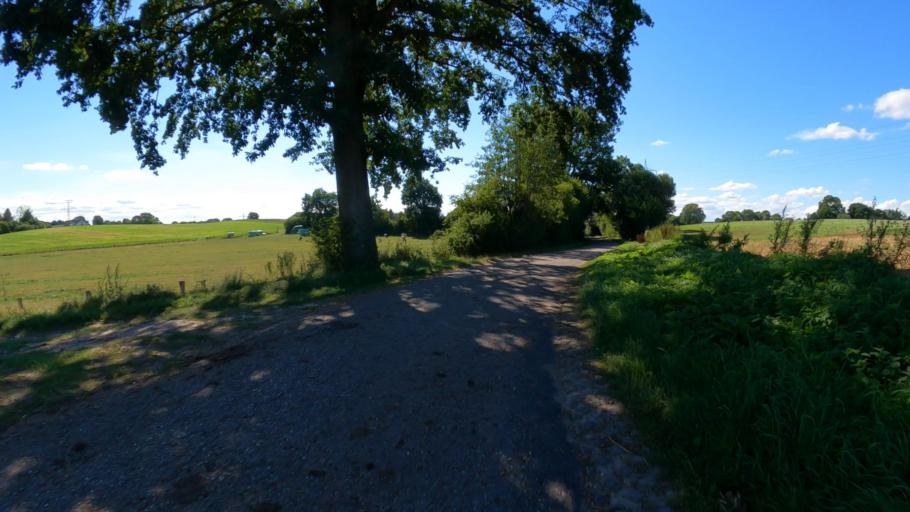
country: DE
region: Schleswig-Holstein
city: Gross Schenkenberg
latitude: 53.8009
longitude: 10.5670
